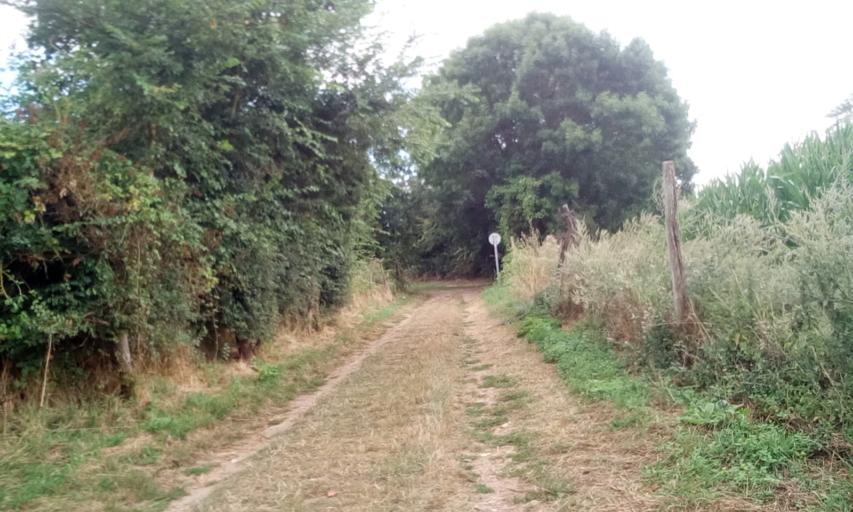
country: FR
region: Lower Normandy
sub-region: Departement du Calvados
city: Bellengreville
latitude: 49.1301
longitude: -0.1939
